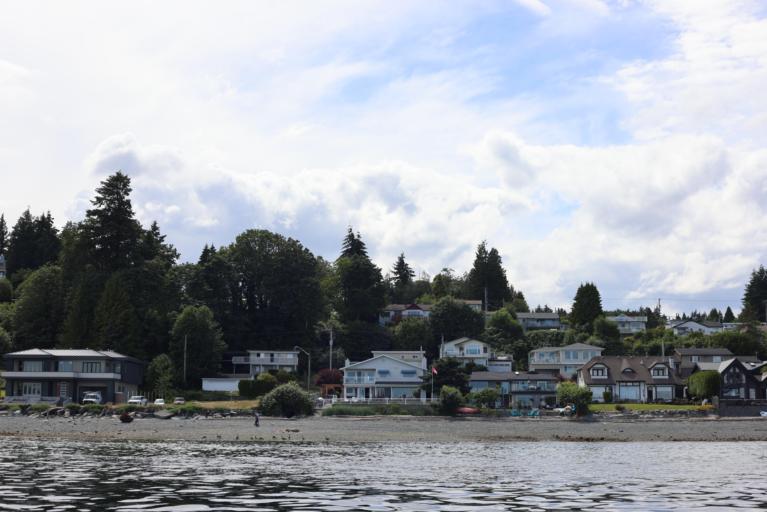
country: CA
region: British Columbia
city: Nanaimo
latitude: 49.2025
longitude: -123.9676
